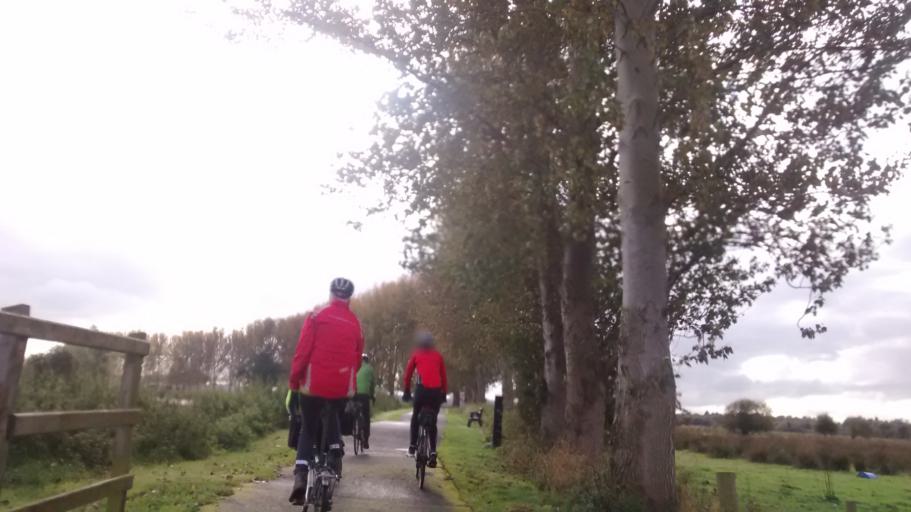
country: GB
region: Northern Ireland
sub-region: Armagh District
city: Portadown
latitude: 54.4197
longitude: -6.4362
